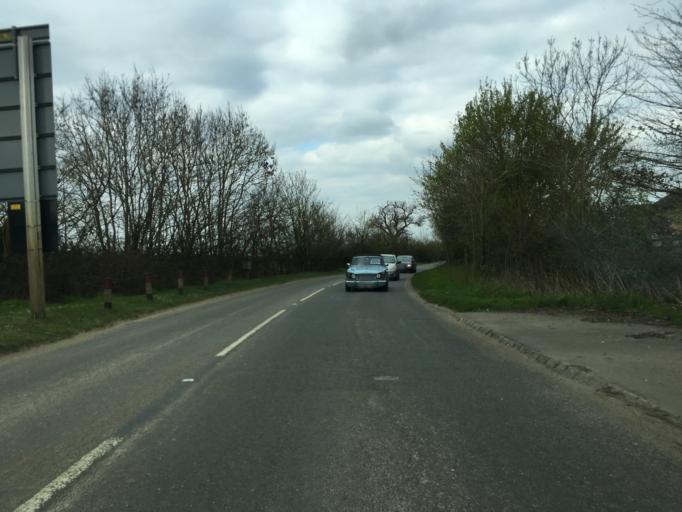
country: GB
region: England
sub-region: Oxfordshire
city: Bicester
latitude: 51.9009
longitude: -1.1814
